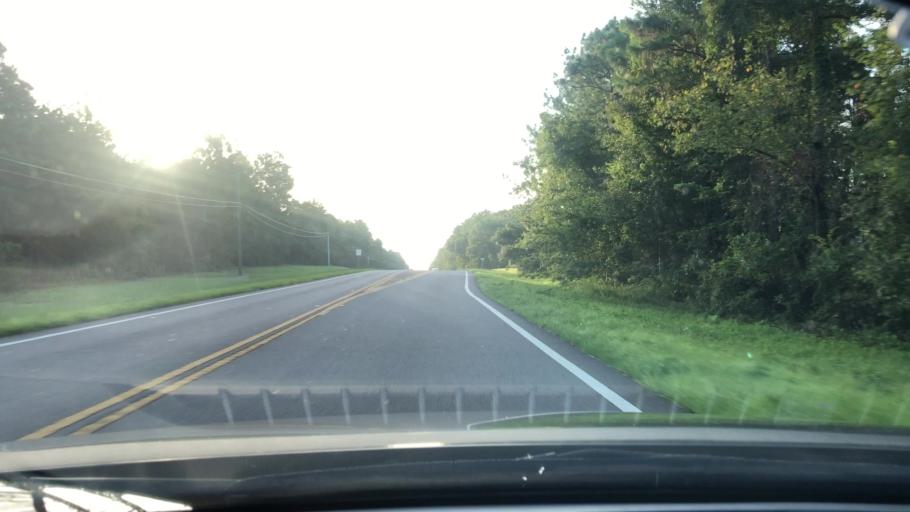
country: US
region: Florida
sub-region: Marion County
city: Belleview
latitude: 29.0262
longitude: -82.2331
